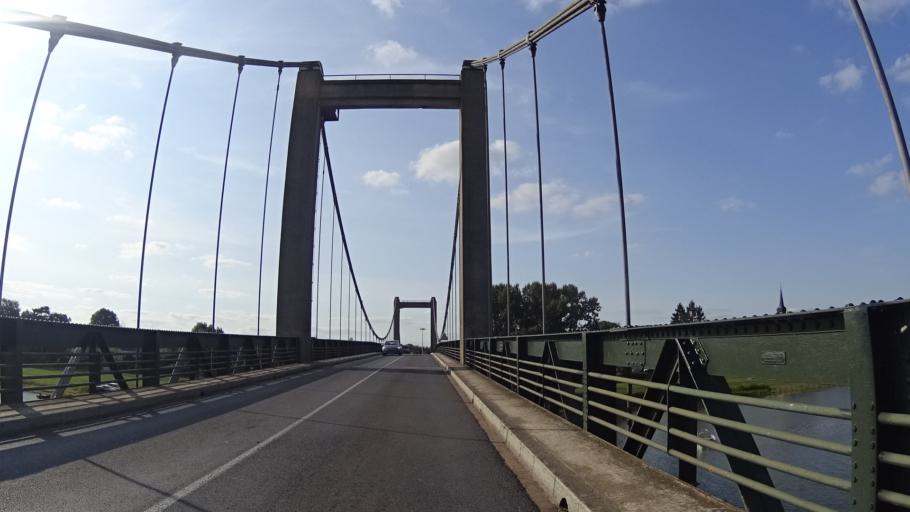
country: FR
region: Pays de la Loire
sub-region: Departement de Maine-et-Loire
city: Bouchemaine
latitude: 47.4200
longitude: -0.6077
